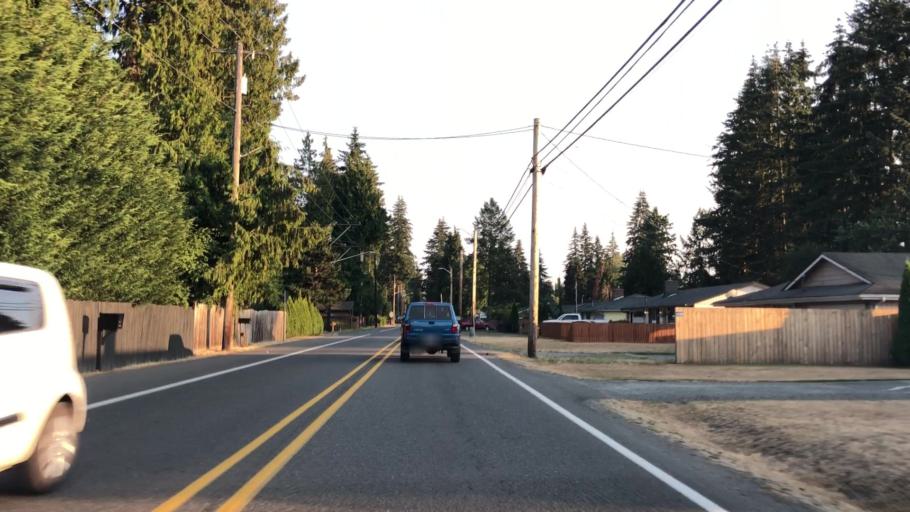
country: US
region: Washington
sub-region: Snohomish County
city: Smokey Point
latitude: 48.1170
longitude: -122.1624
